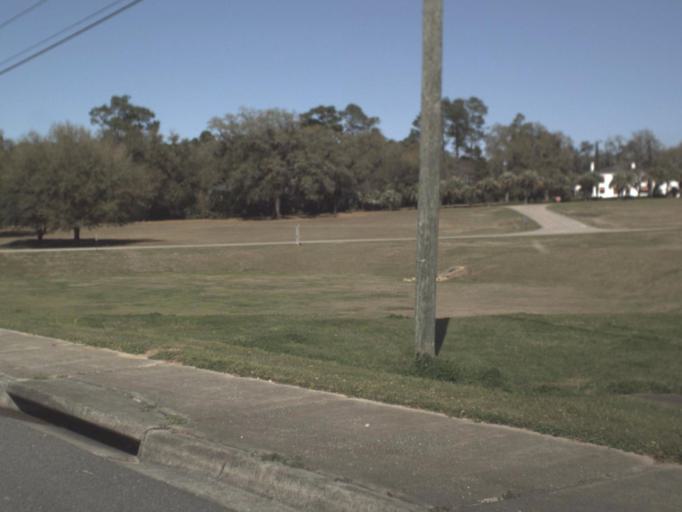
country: US
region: Florida
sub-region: Leon County
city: Tallahassee
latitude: 30.4474
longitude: -84.2264
